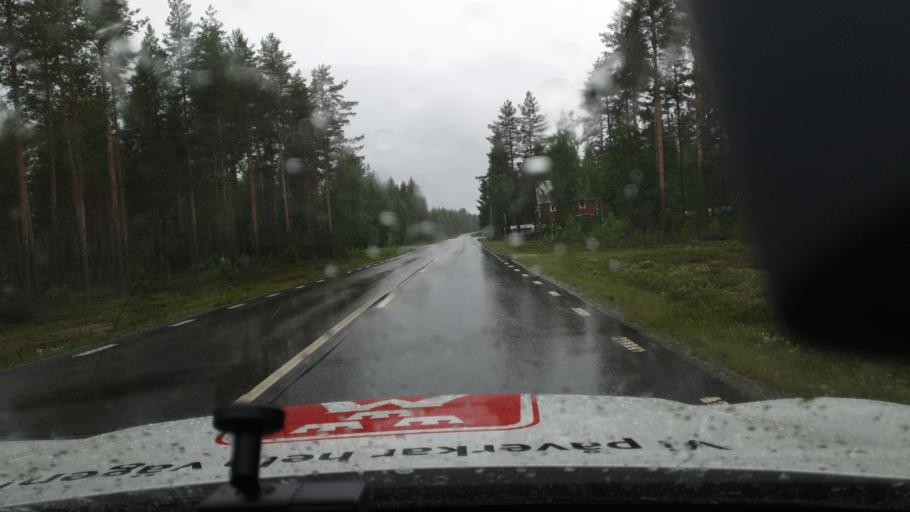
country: SE
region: Vaesterbotten
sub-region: Lycksele Kommun
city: Lycksele
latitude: 64.5291
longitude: 18.7720
